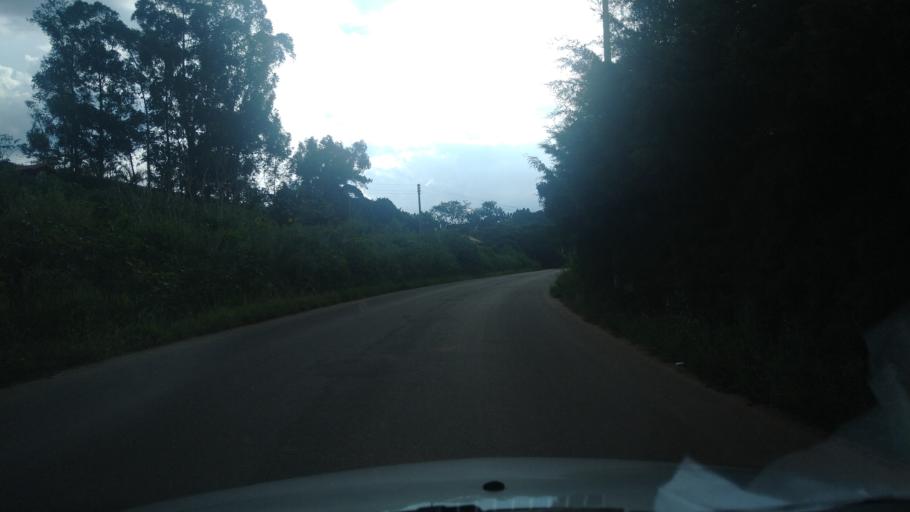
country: BR
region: Minas Gerais
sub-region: Extrema
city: Extrema
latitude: -22.7279
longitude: -46.3553
